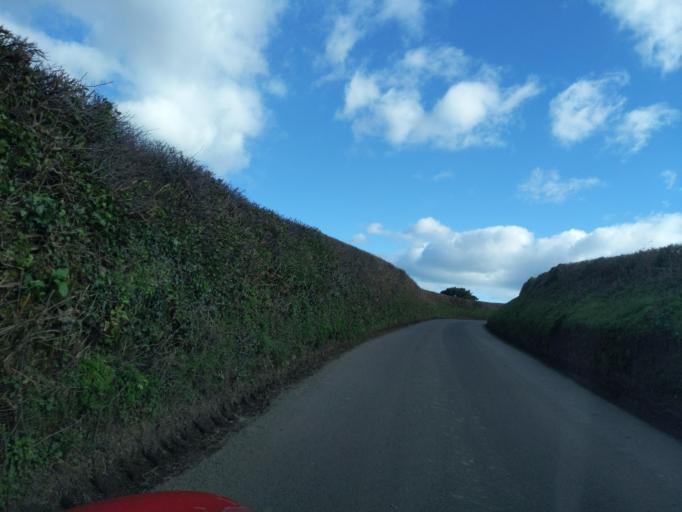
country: GB
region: England
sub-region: Devon
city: Salcombe
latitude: 50.2657
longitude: -3.7204
